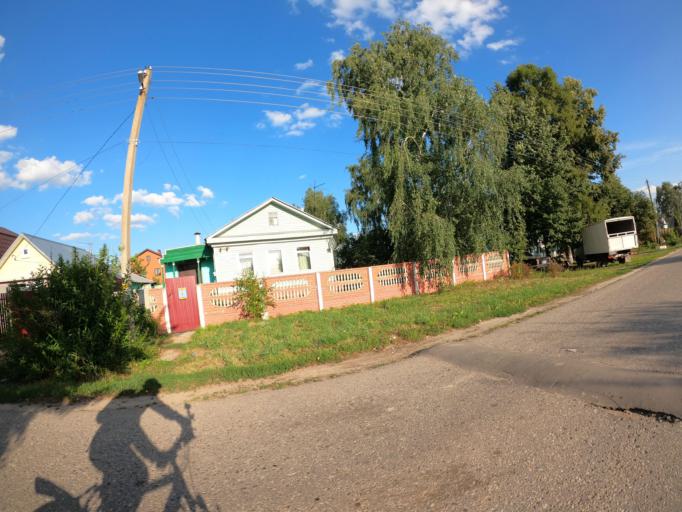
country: RU
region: Moskovskaya
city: Raduzhnyy
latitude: 55.1496
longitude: 38.7363
